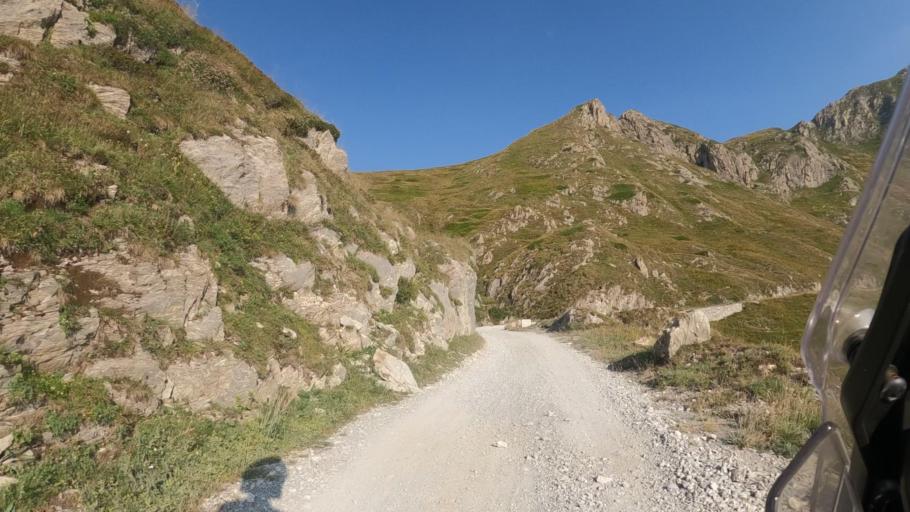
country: IT
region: Piedmont
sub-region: Provincia di Cuneo
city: Limone Piemonte
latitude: 44.1673
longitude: 7.6337
